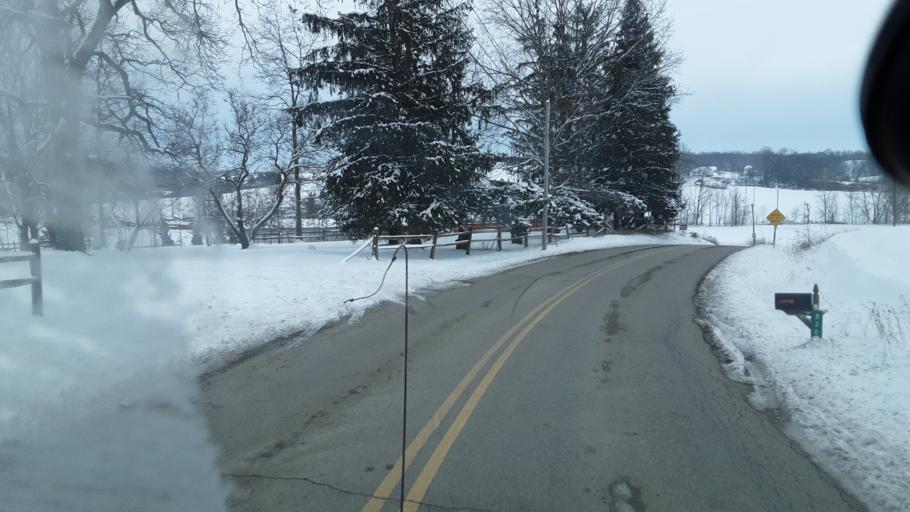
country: US
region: Ohio
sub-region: Perry County
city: Somerset
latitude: 39.9369
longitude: -82.2228
